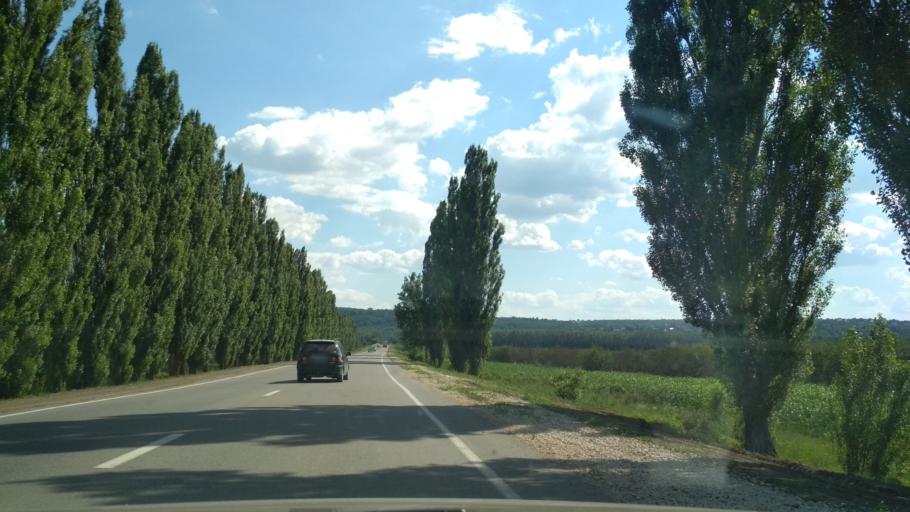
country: MD
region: Chisinau
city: Vadul lui Voda
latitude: 47.0982
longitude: 29.0968
